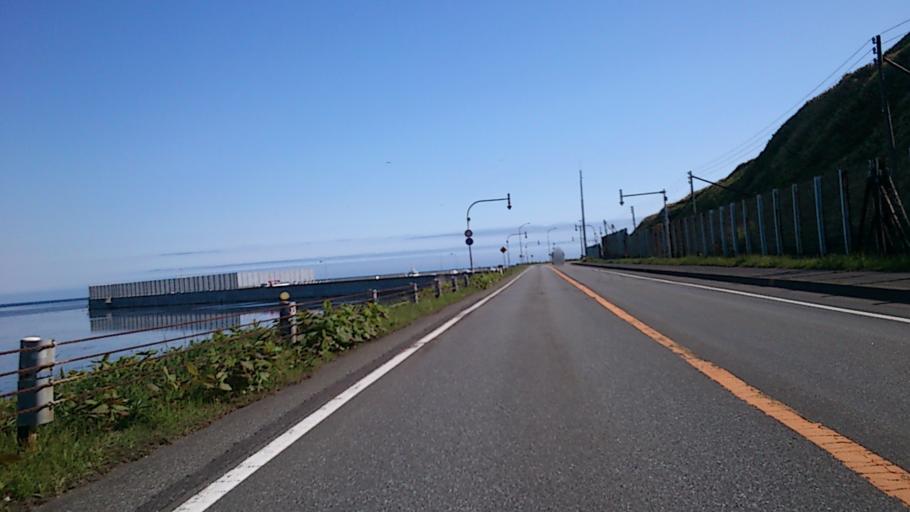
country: JP
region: Hokkaido
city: Makubetsu
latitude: 45.5074
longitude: 141.8931
